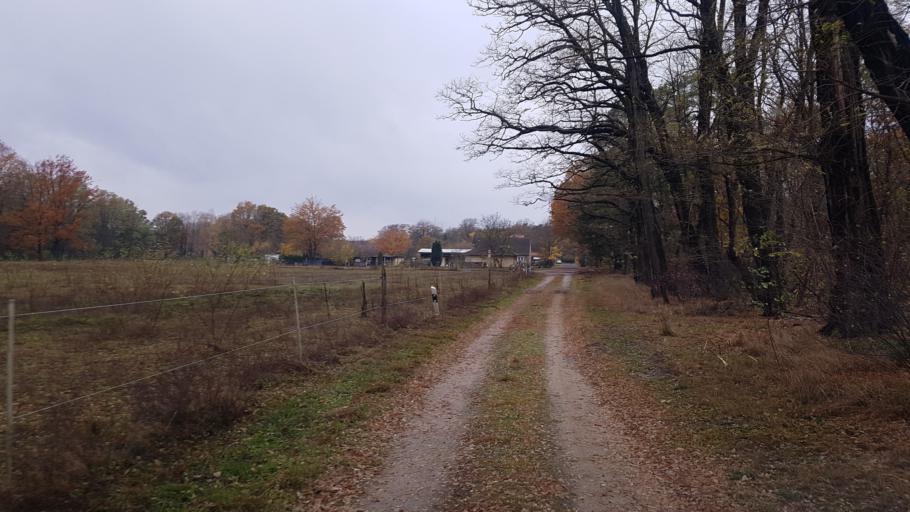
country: DE
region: Brandenburg
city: Drebkau
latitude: 51.6988
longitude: 14.2016
